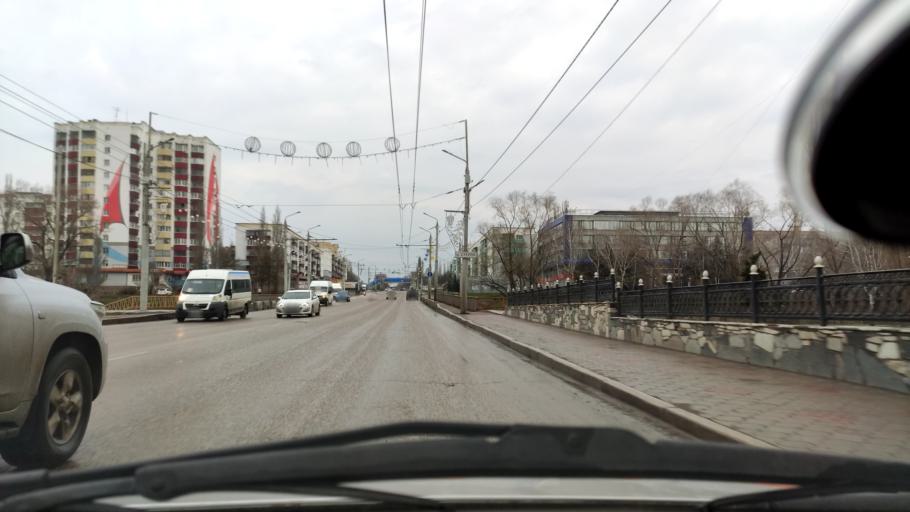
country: RU
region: Bashkortostan
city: Sterlitamak
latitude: 53.6220
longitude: 55.9548
